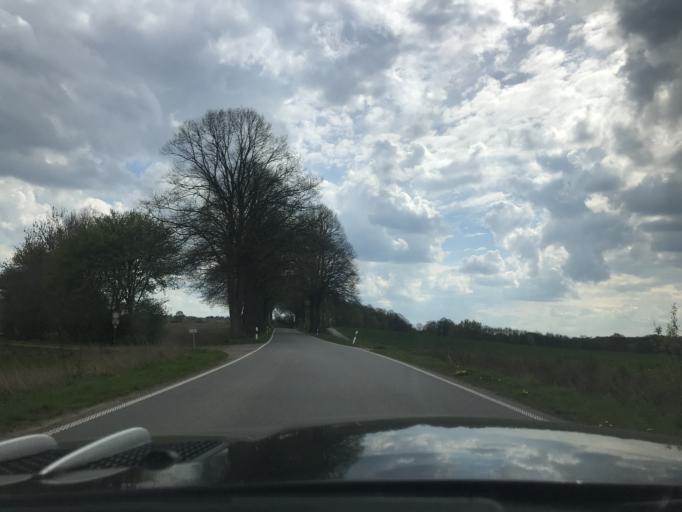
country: DE
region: Schleswig-Holstein
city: Timmendorfer Strand
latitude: 53.9460
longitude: 10.7894
